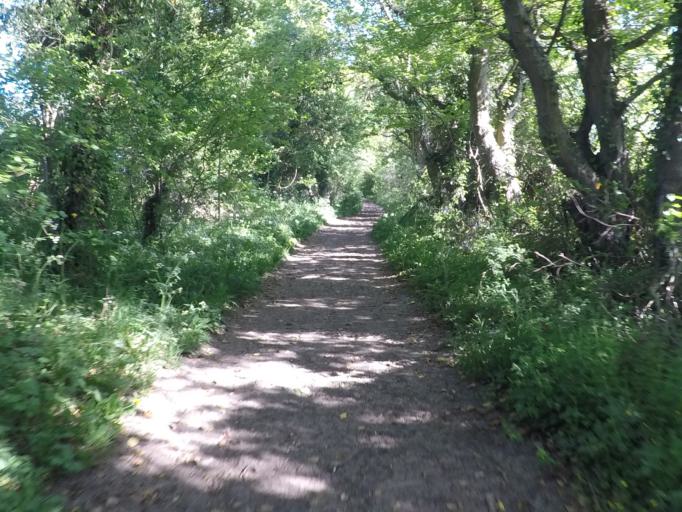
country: GB
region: England
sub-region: Oxfordshire
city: Charlbury
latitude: 51.8636
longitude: -1.4692
